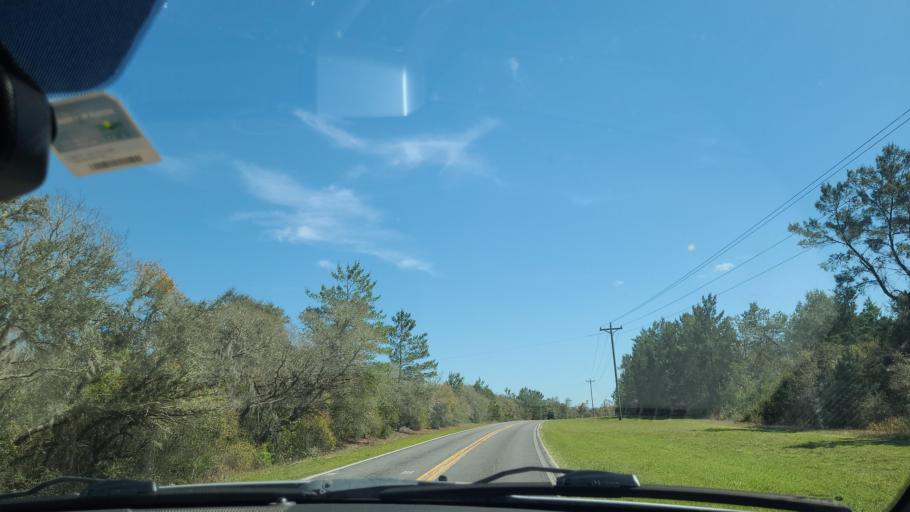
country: US
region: Florida
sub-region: Marion County
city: Citra
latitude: 29.4043
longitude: -81.8972
